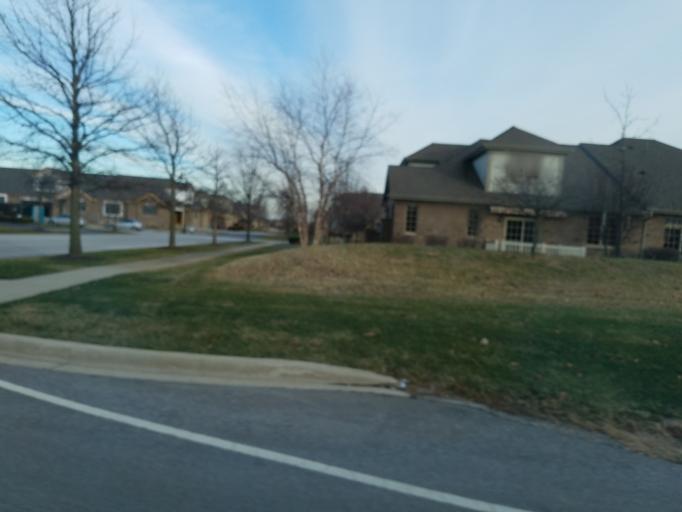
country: US
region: Illinois
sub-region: Will County
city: Goodings Grove
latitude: 41.6210
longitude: -87.9501
